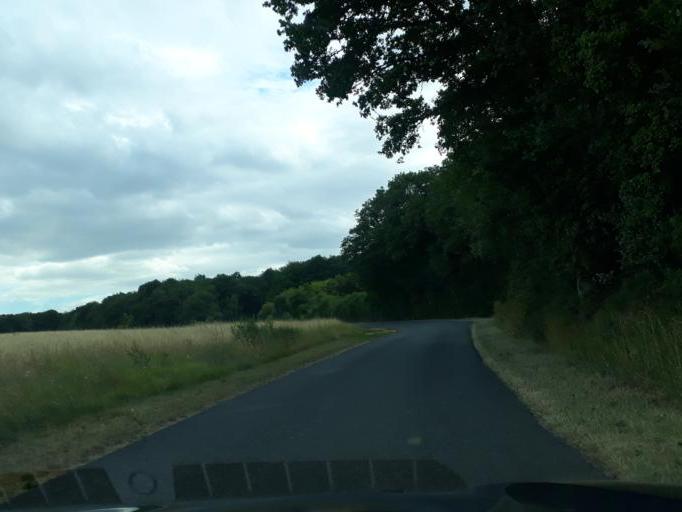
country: FR
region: Centre
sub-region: Departement du Loir-et-Cher
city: Ouzouer-le-Marche
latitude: 47.8738
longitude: 1.4137
